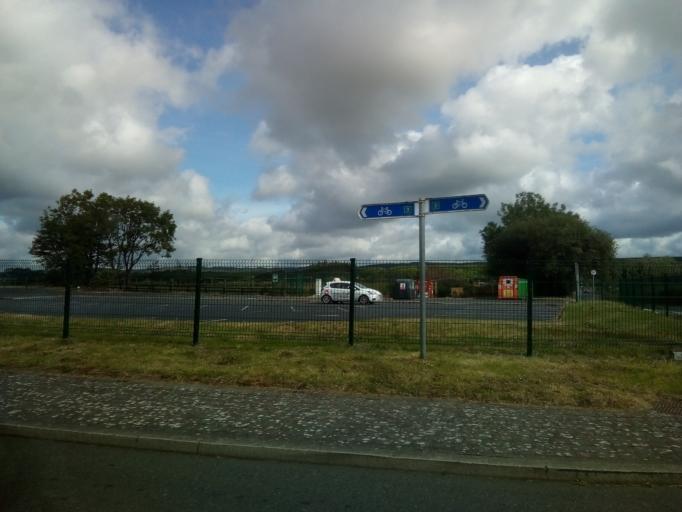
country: IE
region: Leinster
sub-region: Loch Garman
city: Loch Garman
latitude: 52.2872
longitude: -6.5204
